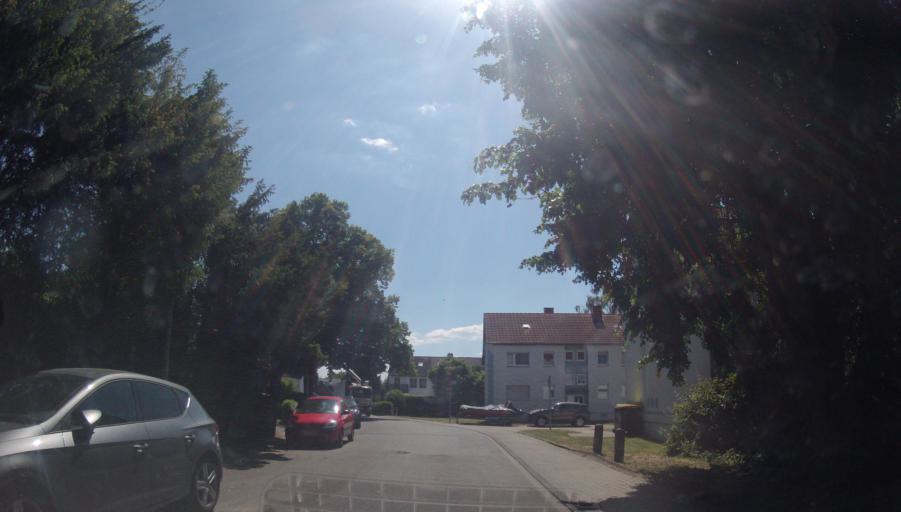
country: DE
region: North Rhine-Westphalia
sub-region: Regierungsbezirk Dusseldorf
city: Muelheim (Ruhr)
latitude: 51.4048
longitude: 6.8515
